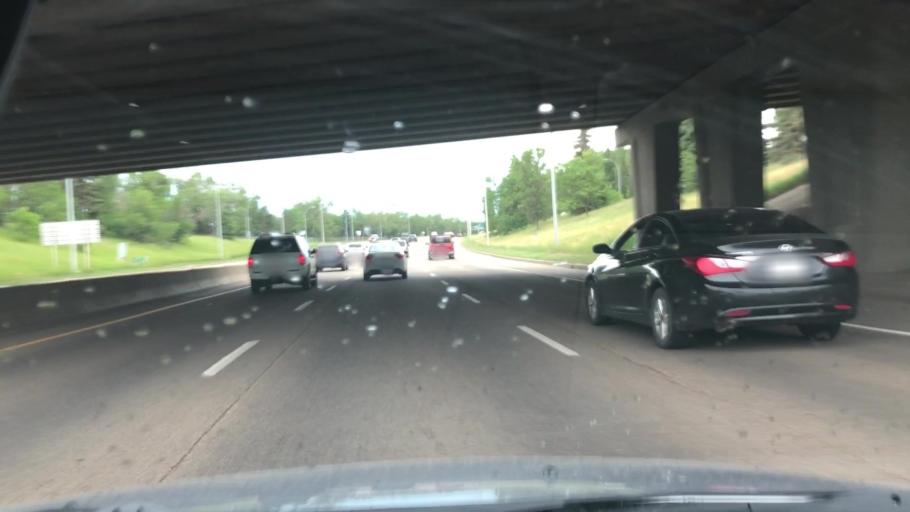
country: CA
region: Alberta
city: Edmonton
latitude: 53.5627
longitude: -113.4462
